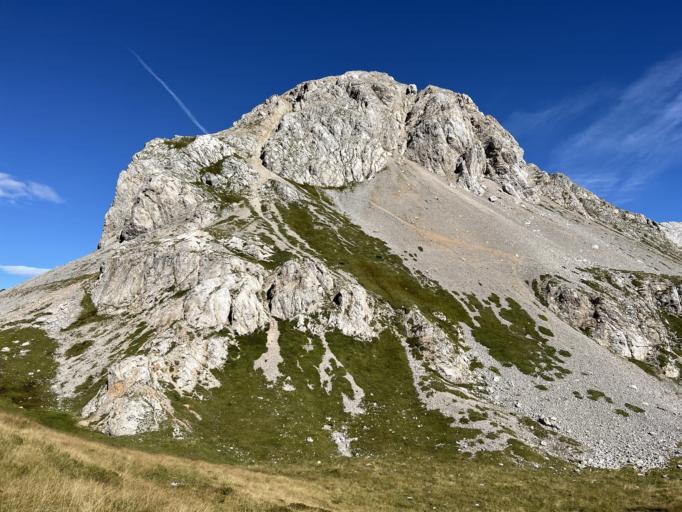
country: IT
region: Friuli Venezia Giulia
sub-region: Provincia di Udine
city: Forni Avoltri
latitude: 46.6289
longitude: 12.8150
